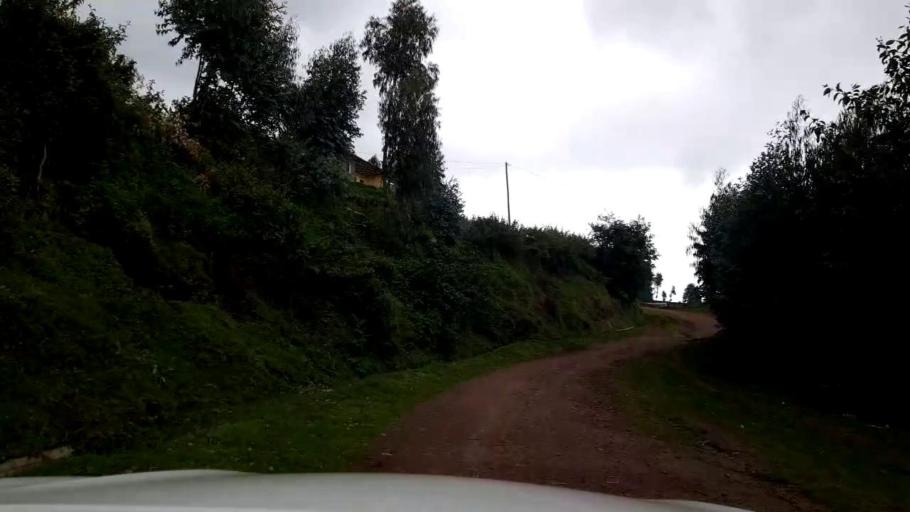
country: RW
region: Western Province
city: Gisenyi
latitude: -1.6756
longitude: 29.4128
